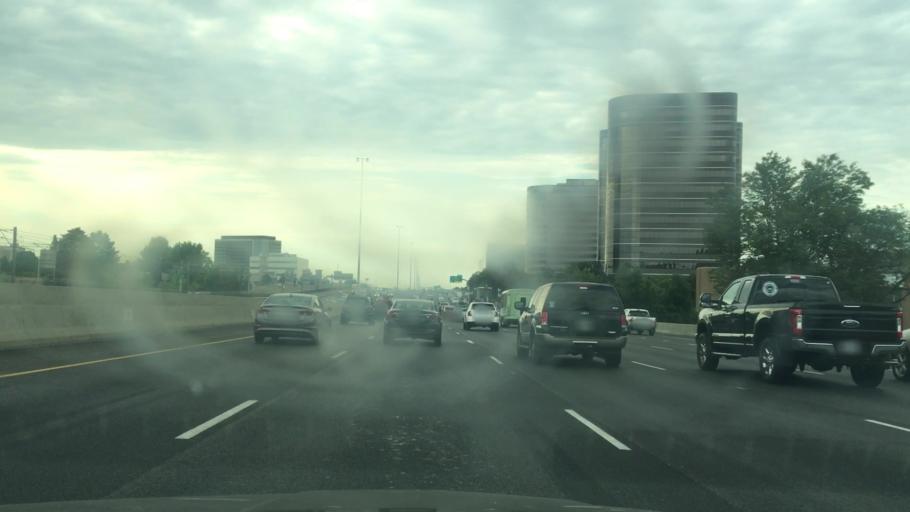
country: US
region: Colorado
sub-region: Arapahoe County
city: Castlewood
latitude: 39.6162
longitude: -104.8963
